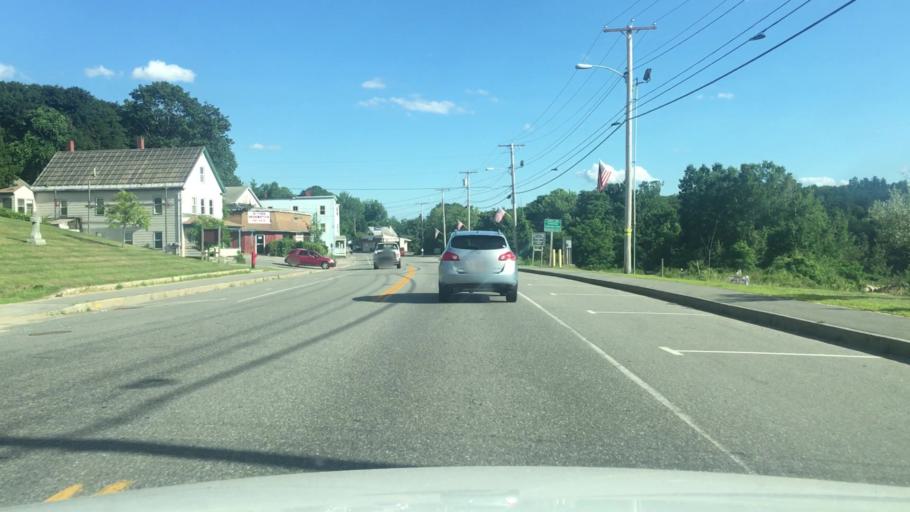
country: US
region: Maine
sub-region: Franklin County
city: Chisholm
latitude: 44.4792
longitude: -70.1966
